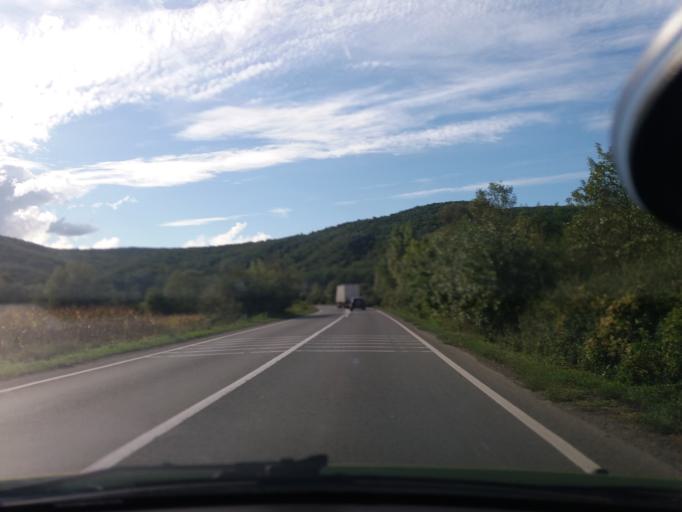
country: RO
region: Arad
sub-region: Comuna Barzava
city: Barzava
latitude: 46.1127
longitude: 21.9623
